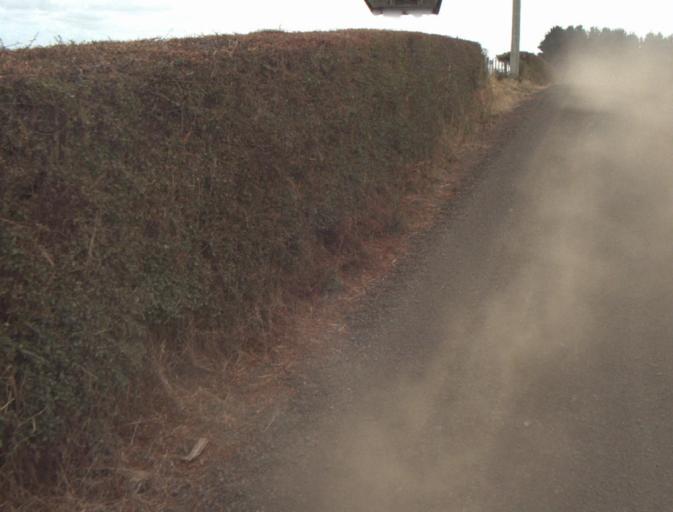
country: AU
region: Tasmania
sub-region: Northern Midlands
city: Evandale
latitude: -41.5224
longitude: 147.2643
